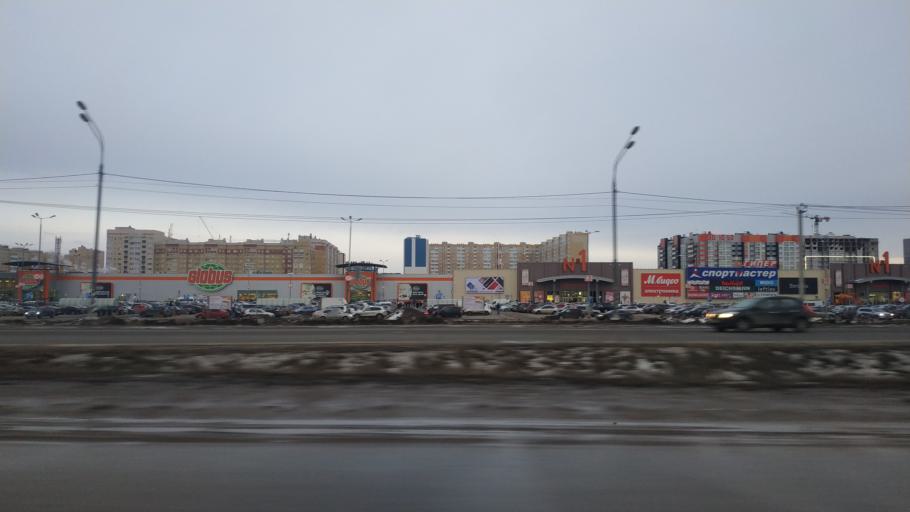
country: RU
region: Tverskaya
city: Tver
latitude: 56.8167
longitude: 35.8821
